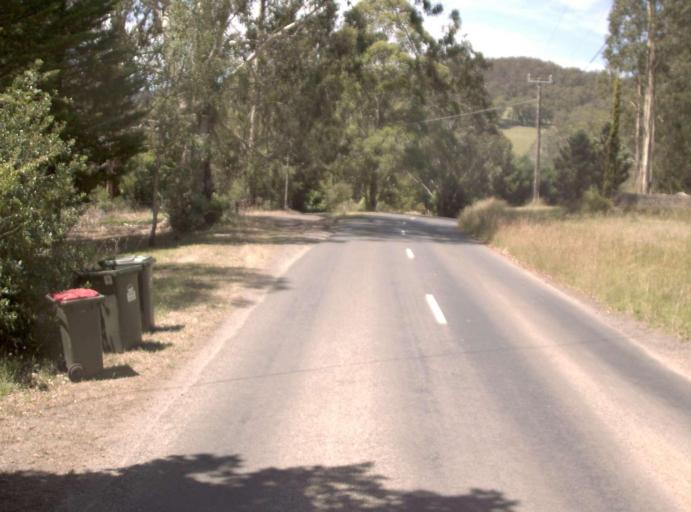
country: AU
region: Victoria
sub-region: Baw Baw
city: Warragul
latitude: -37.8937
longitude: 145.9942
